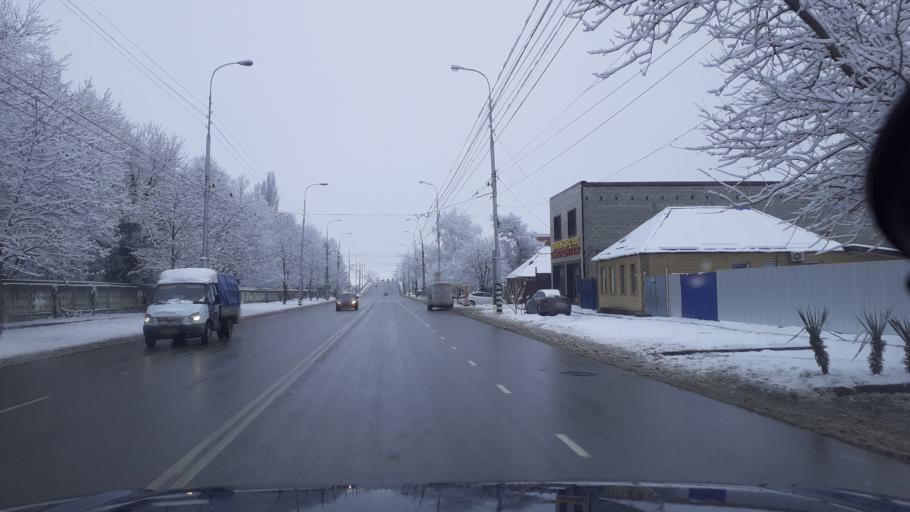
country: RU
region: Adygeya
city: Maykop
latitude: 44.6167
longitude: 40.1209
